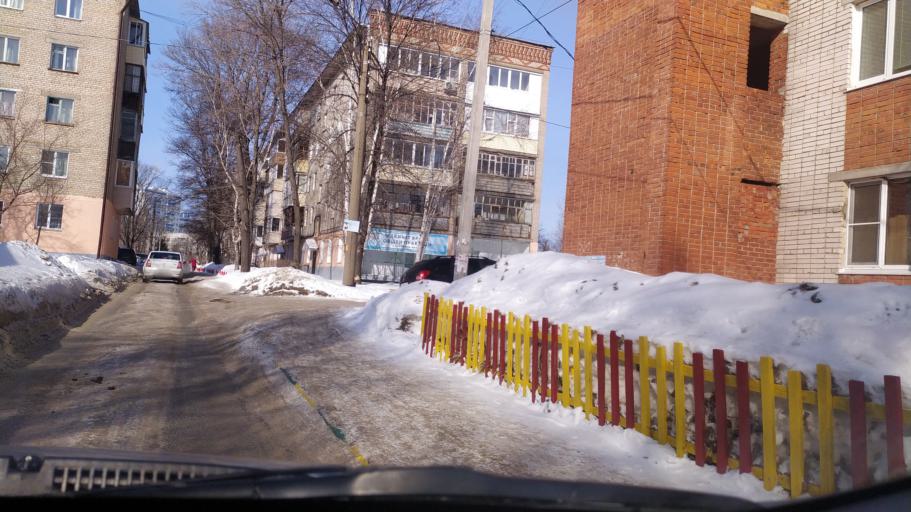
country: RU
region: Chuvashia
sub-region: Cheboksarskiy Rayon
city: Cheboksary
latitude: 56.1489
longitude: 47.2244
